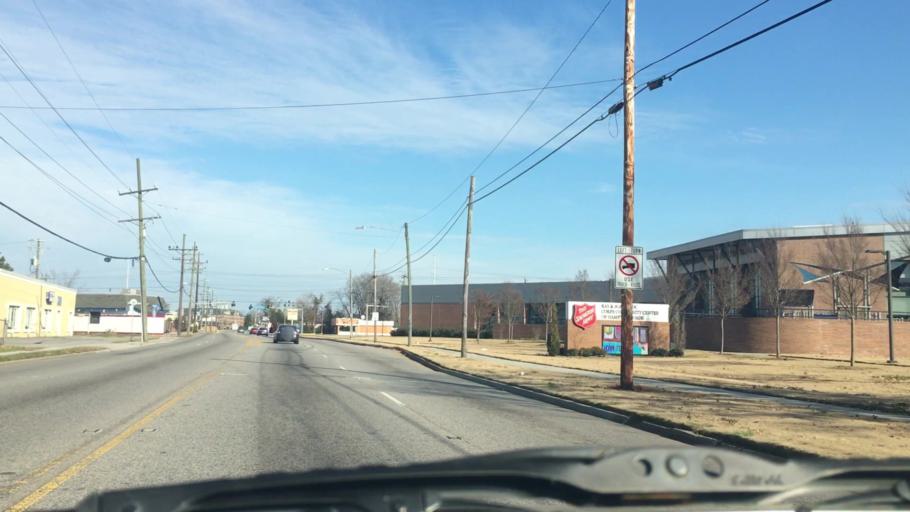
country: US
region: Virginia
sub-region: City of Norfolk
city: Norfolk
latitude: 36.8590
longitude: -76.2513
